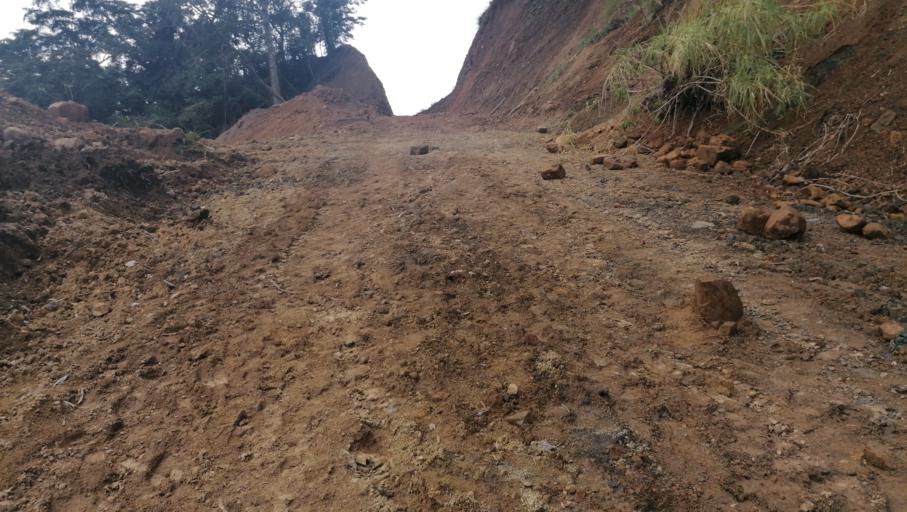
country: MX
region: Chiapas
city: Ostuacan
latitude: 17.3580
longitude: -93.3210
